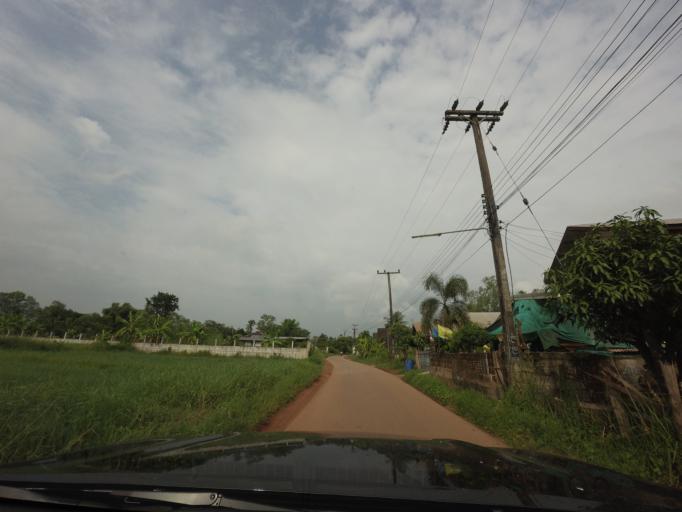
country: TH
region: Nong Khai
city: Nong Khai
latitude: 17.8151
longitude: 102.7219
